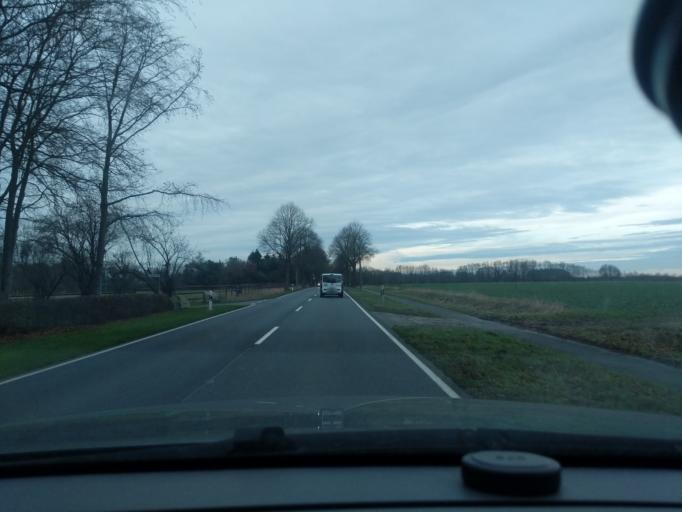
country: DE
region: Lower Saxony
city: Beckdorf
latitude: 53.4037
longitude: 9.6102
